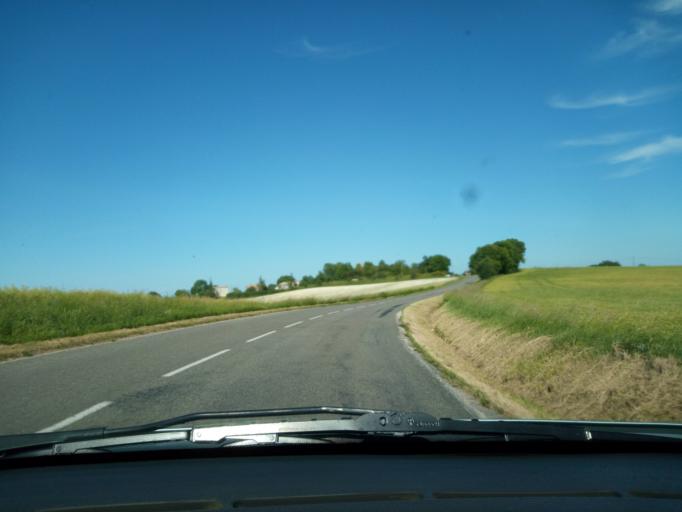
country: FR
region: Midi-Pyrenees
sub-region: Departement du Lot
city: Castelnau-Montratier
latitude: 44.3090
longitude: 1.4225
